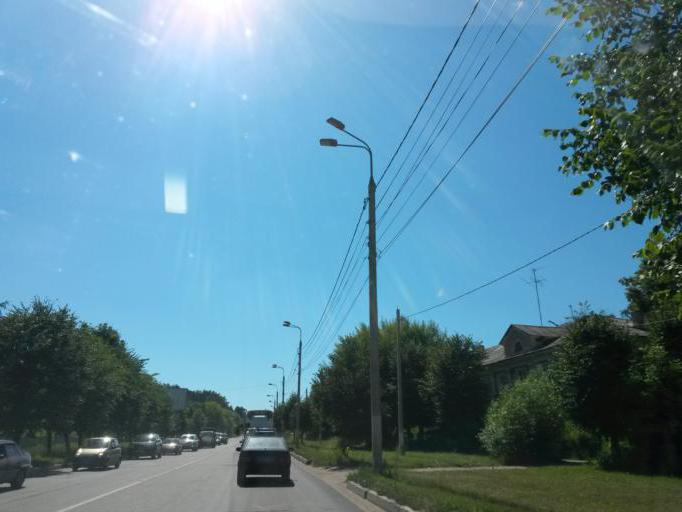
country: RU
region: Moskovskaya
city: Serpukhov
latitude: 54.9098
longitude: 37.3853
